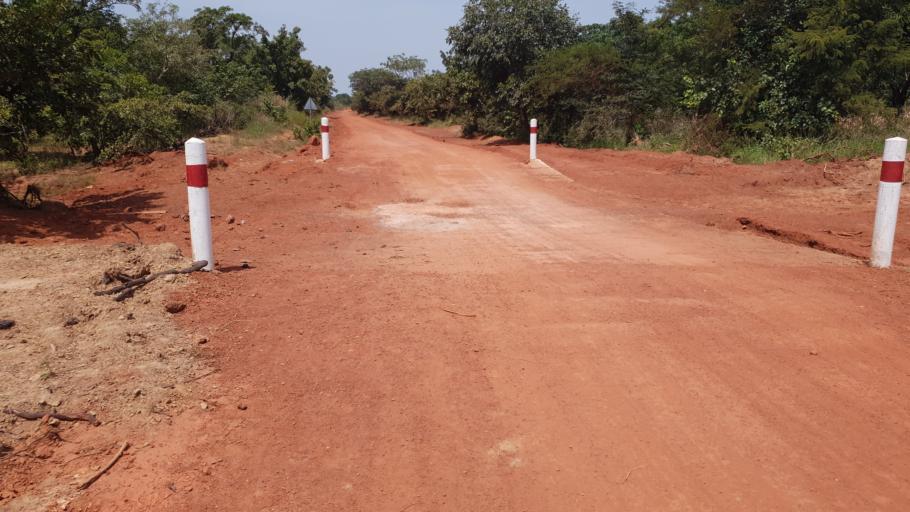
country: ML
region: Sikasso
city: Sikasso
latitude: 11.5945
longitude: -6.3452
